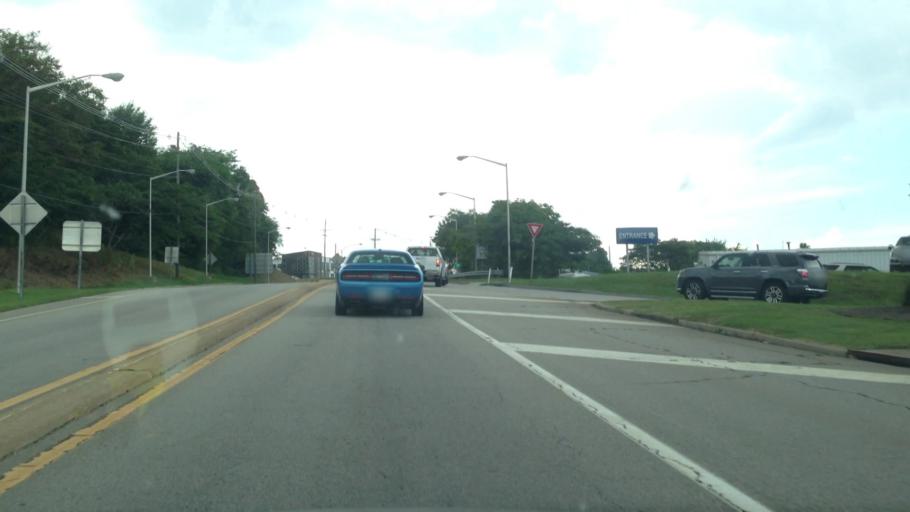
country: US
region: Virginia
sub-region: City of Danville
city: Danville
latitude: 36.5817
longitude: -79.4329
